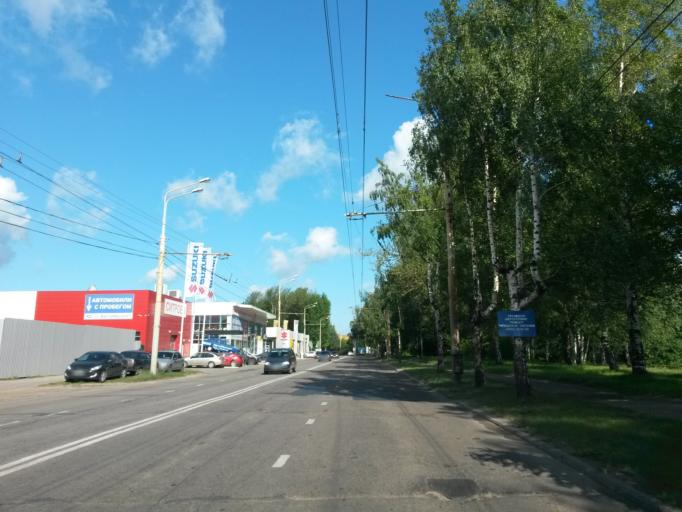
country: RU
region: Jaroslavl
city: Yaroslavl
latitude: 57.6593
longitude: 39.8624
